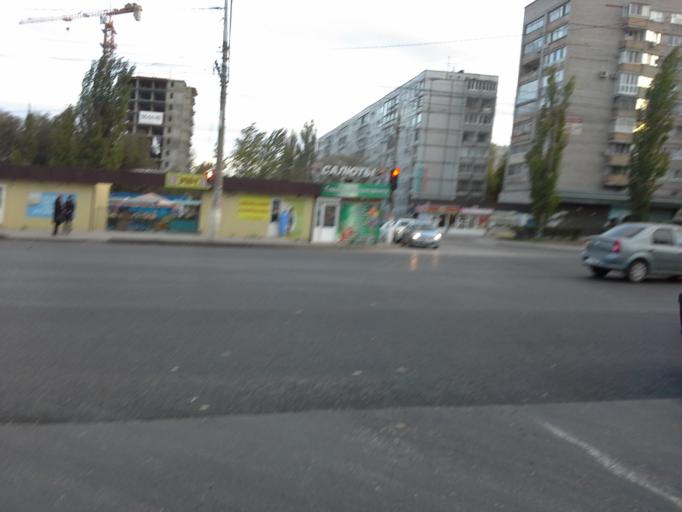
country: RU
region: Volgograd
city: Vodstroy
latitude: 48.8201
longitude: 44.6333
